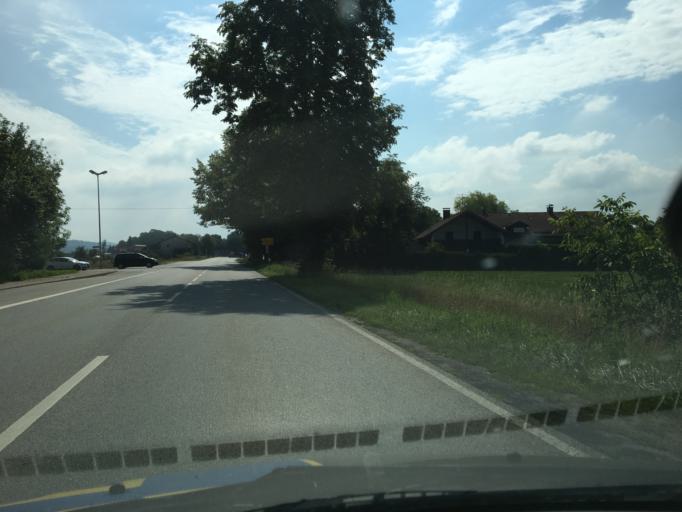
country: DE
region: Bavaria
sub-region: Upper Bavaria
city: Aresing
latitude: 48.2707
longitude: 12.6048
